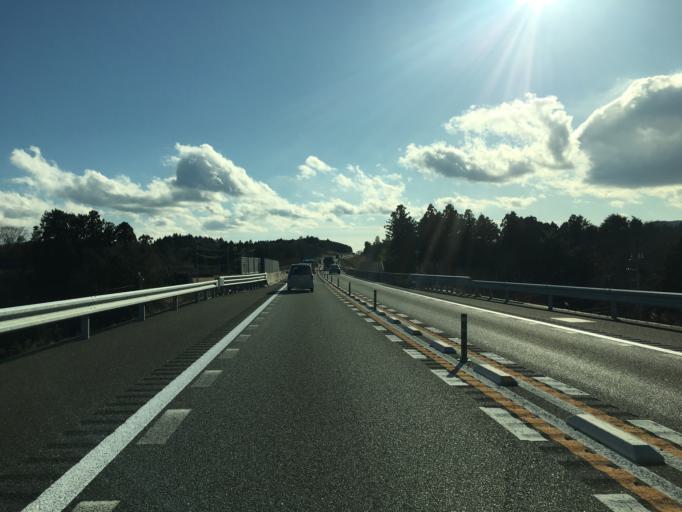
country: JP
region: Fukushima
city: Namie
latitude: 37.5597
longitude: 140.9455
